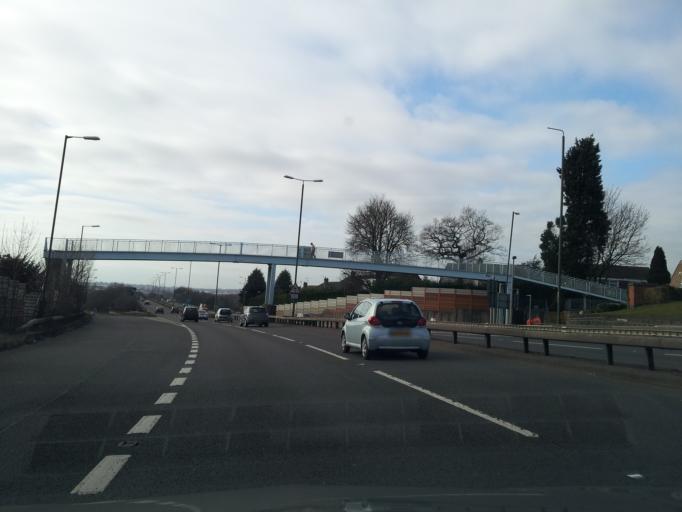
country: GB
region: England
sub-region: Derbyshire
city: Borrowash
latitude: 52.9174
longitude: -1.4083
